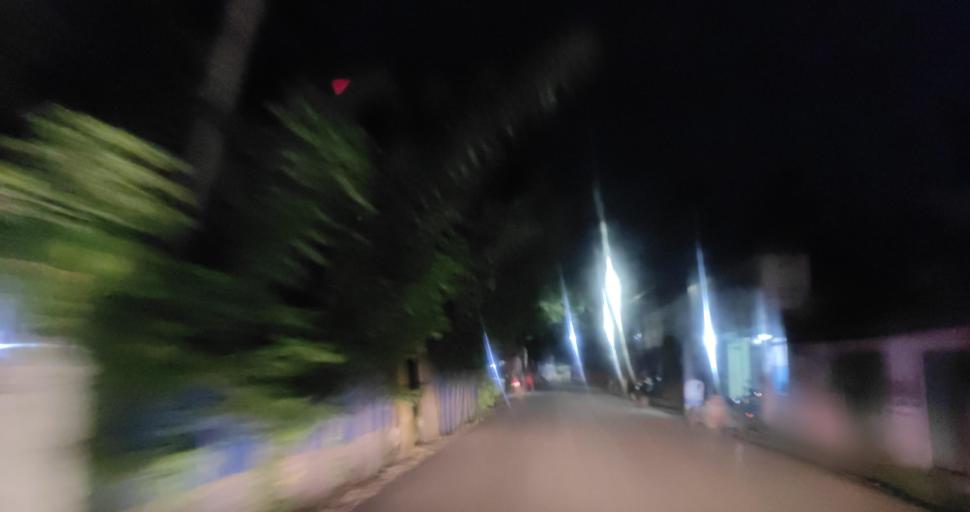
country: IN
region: Kerala
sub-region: Alappuzha
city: Vayalar
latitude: 9.6846
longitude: 76.3024
